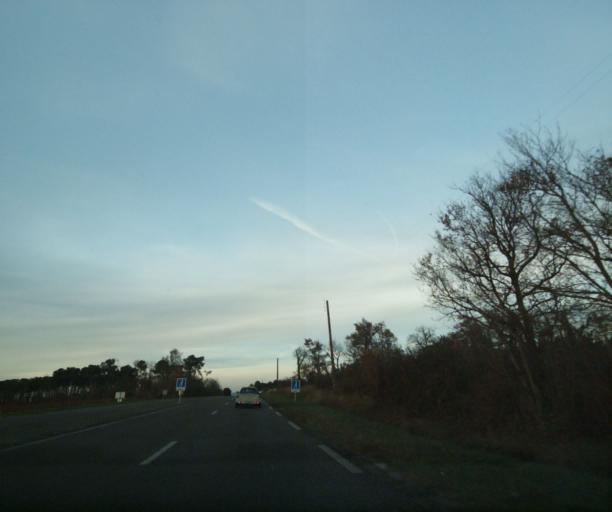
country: FR
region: Aquitaine
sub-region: Departement de la Gironde
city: Langon
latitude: 44.5103
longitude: -0.2388
